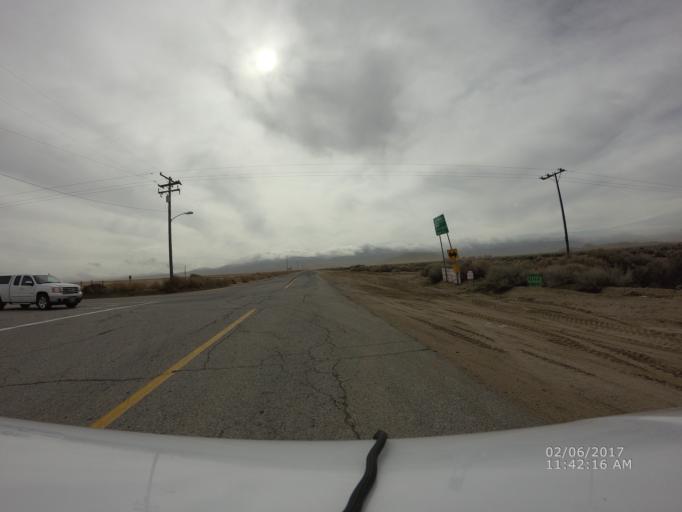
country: US
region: California
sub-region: Los Angeles County
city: Lake Los Angeles
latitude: 34.6020
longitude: -117.7025
